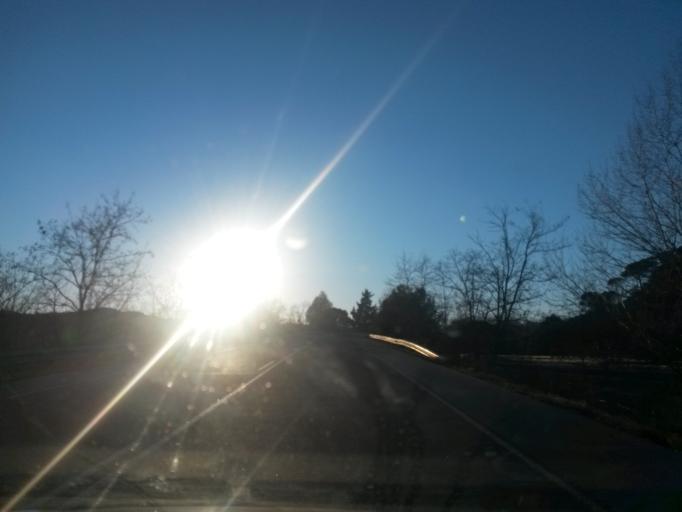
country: ES
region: Catalonia
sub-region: Provincia de Girona
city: Massanes
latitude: 41.7435
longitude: 2.6785
